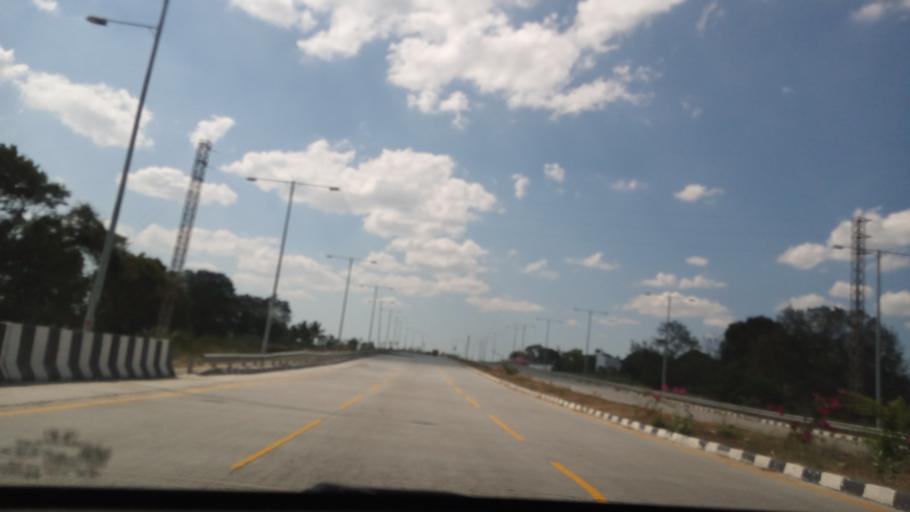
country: IN
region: Andhra Pradesh
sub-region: Chittoor
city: Palmaner
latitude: 13.2147
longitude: 78.7473
